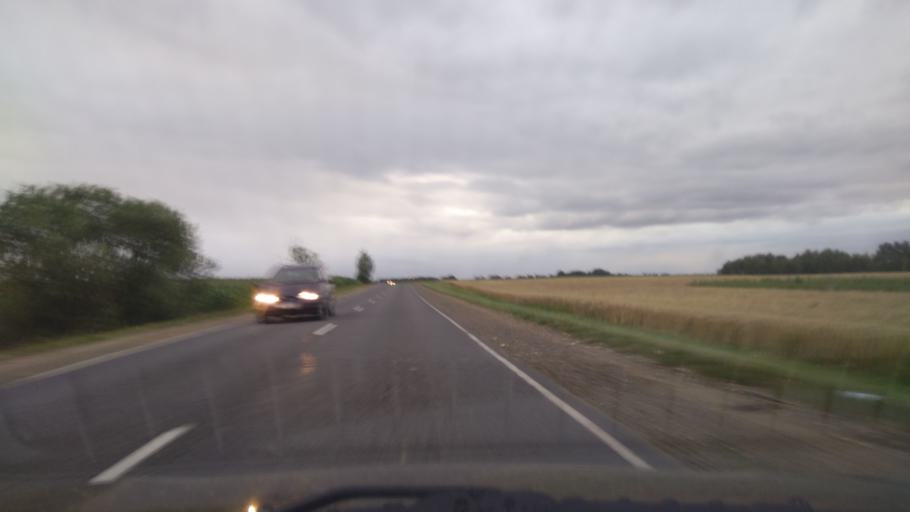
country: BY
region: Brest
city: Byaroza
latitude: 52.4286
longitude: 24.9808
